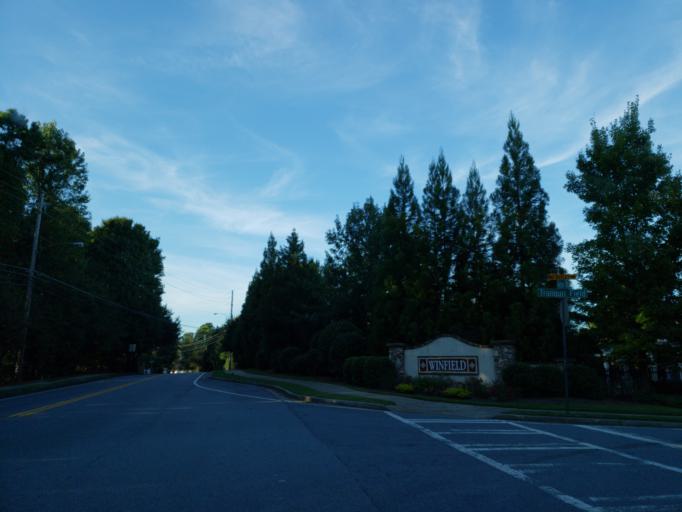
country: US
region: Georgia
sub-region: Cobb County
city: Kennesaw
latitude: 34.0666
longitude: -84.6059
